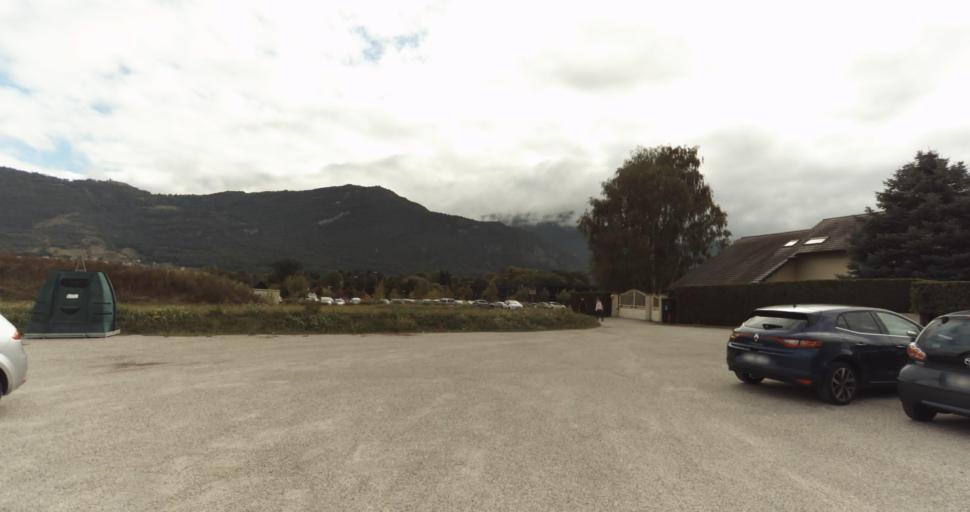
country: FR
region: Rhone-Alpes
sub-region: Departement de la Savoie
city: La Ravoire
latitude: 45.5471
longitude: 5.9690
